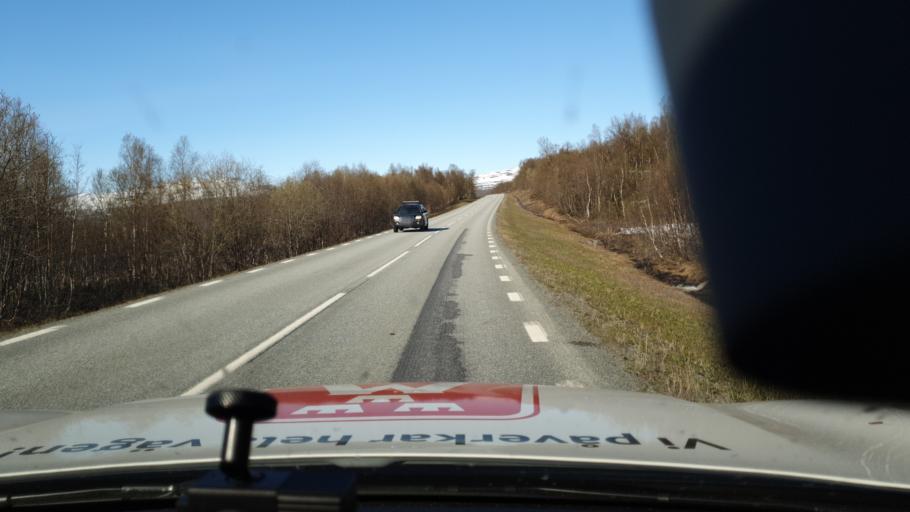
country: NO
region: Nordland
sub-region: Rana
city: Mo i Rana
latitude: 65.9901
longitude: 15.0703
